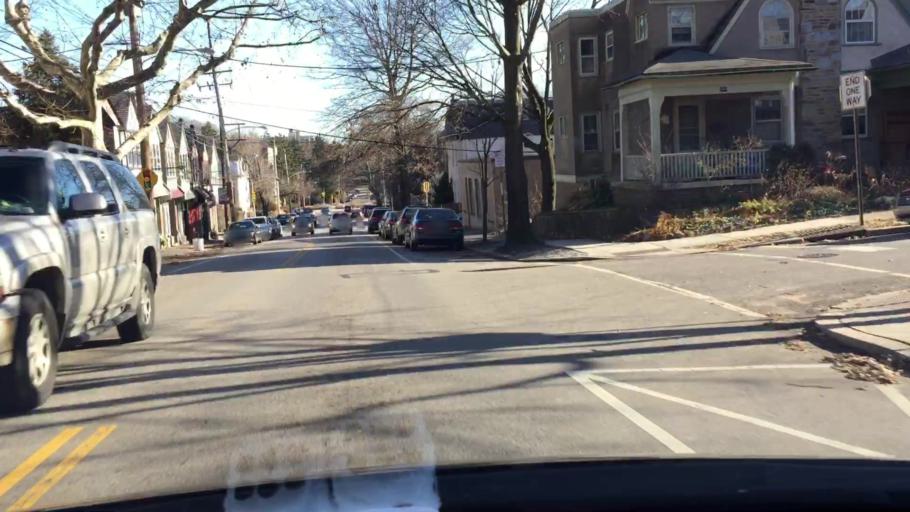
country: US
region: Pennsylvania
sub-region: Montgomery County
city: Wyndmoor
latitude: 40.0537
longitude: -75.1970
